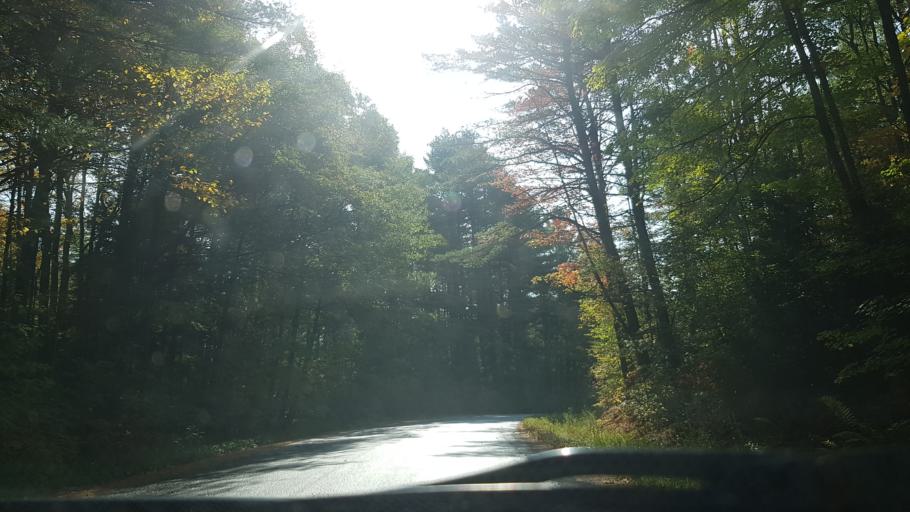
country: CA
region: Ontario
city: Bracebridge
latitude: 44.9790
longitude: -79.2609
